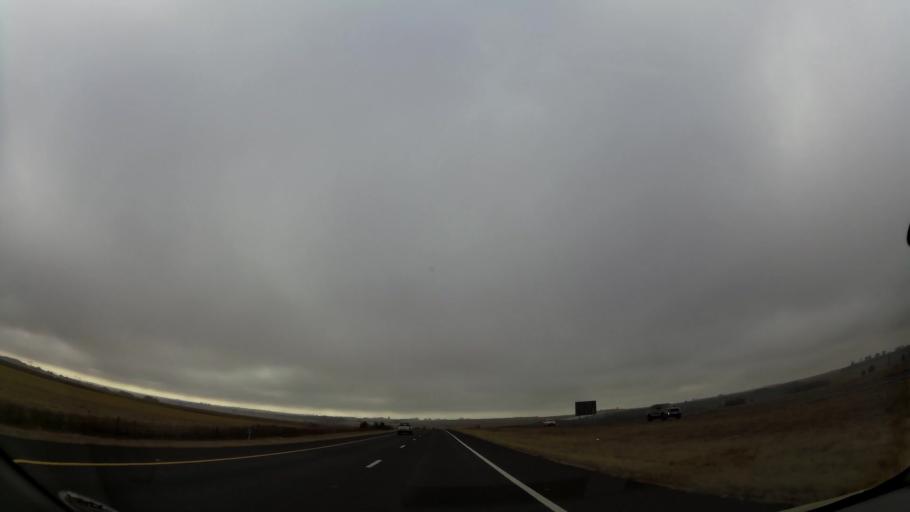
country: ZA
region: Mpumalanga
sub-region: Nkangala District Municipality
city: Delmas
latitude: -26.0687
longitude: 28.7714
